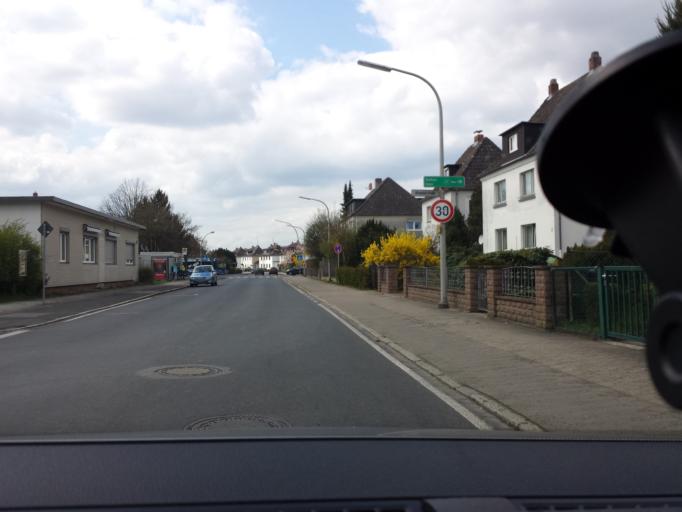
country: DE
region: Lower Saxony
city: Braunschweig
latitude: 52.2791
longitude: 10.4842
